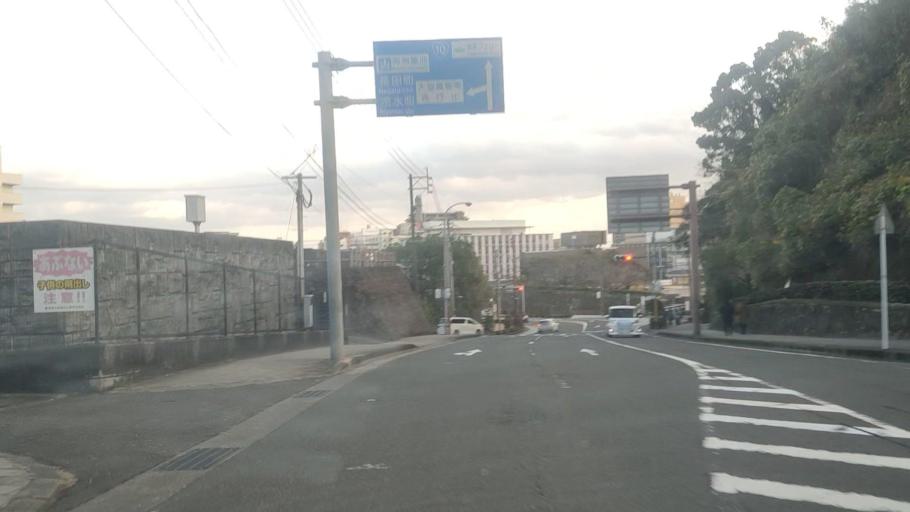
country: JP
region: Kagoshima
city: Kagoshima-shi
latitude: 31.6006
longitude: 130.5546
